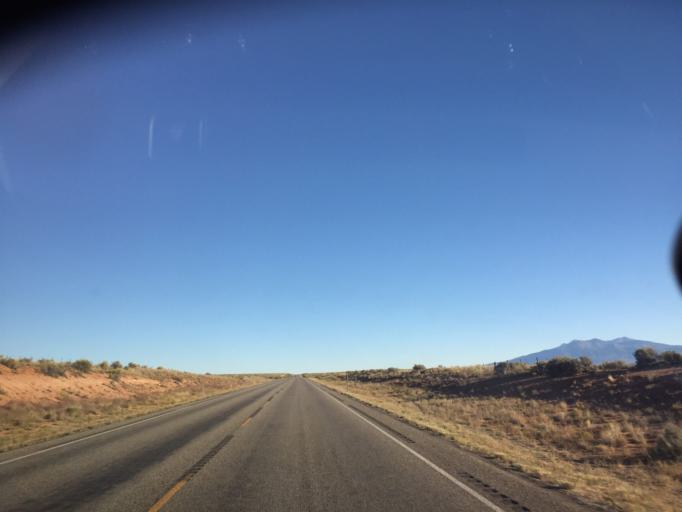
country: US
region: Utah
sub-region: San Juan County
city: Monticello
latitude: 38.1194
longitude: -109.3664
